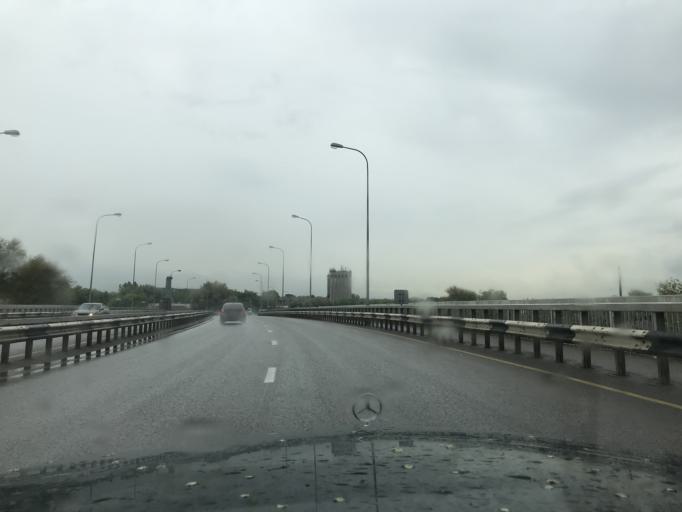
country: KZ
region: Almaty Oblysy
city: Pervomayskiy
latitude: 43.3369
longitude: 76.9635
